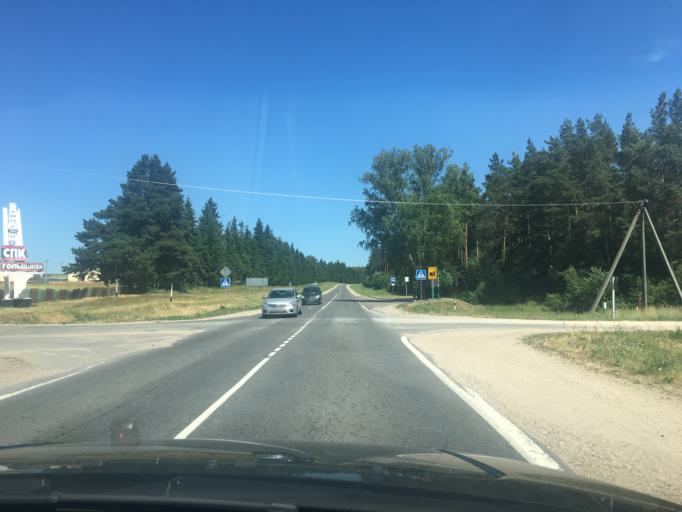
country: BY
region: Grodnenskaya
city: Hal'shany
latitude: 54.2158
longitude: 25.9685
